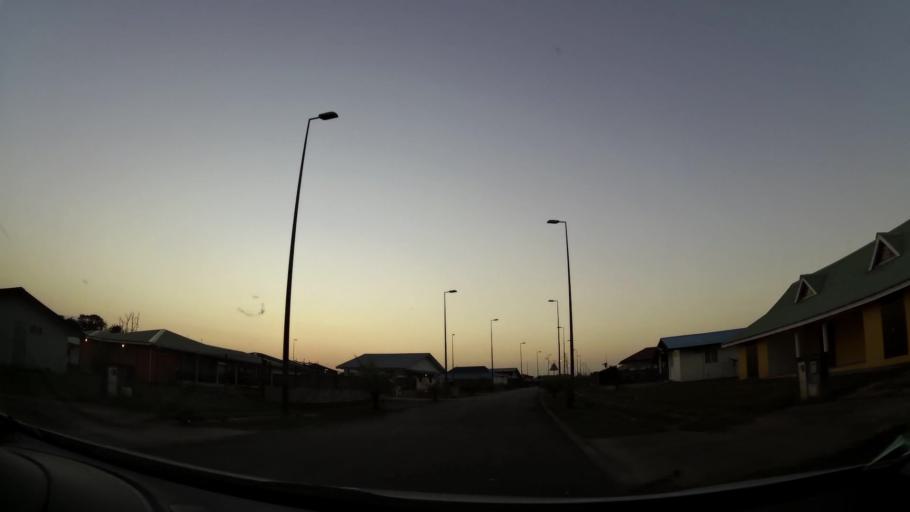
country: GF
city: Macouria
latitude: 4.9230
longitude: -52.4070
